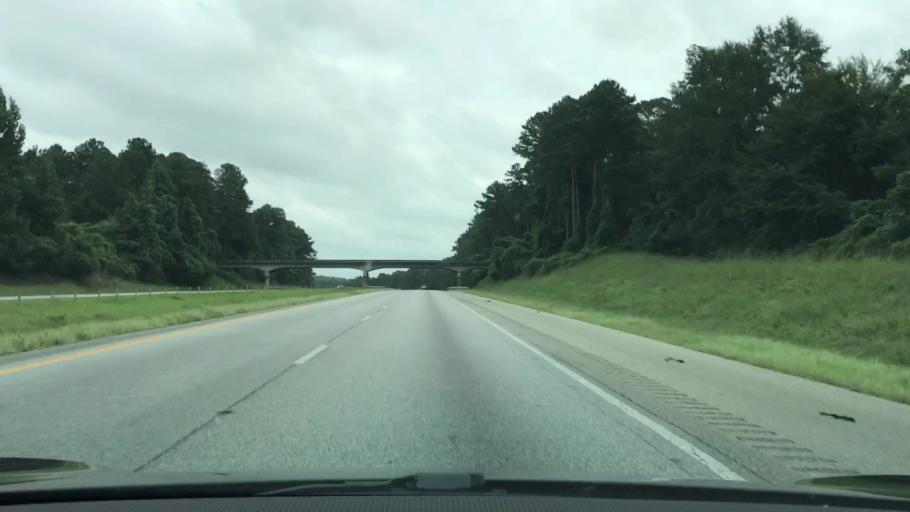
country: US
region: Alabama
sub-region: Macon County
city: Tuskegee
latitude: 32.5133
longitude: -85.5875
